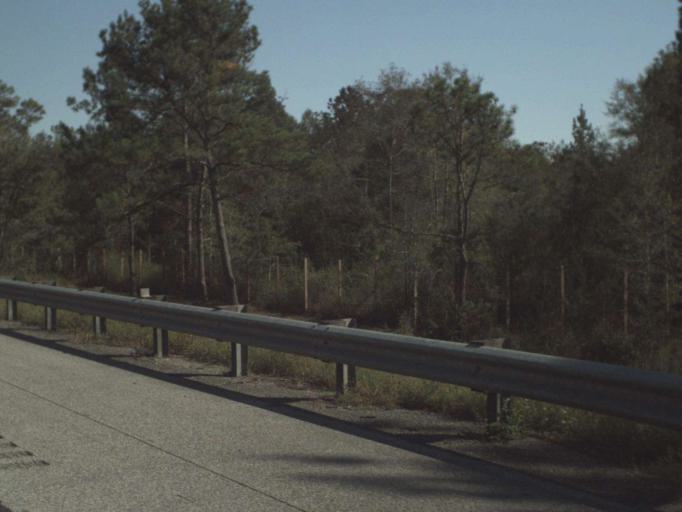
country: US
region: Florida
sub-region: Holmes County
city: Bonifay
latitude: 30.7547
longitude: -85.6115
